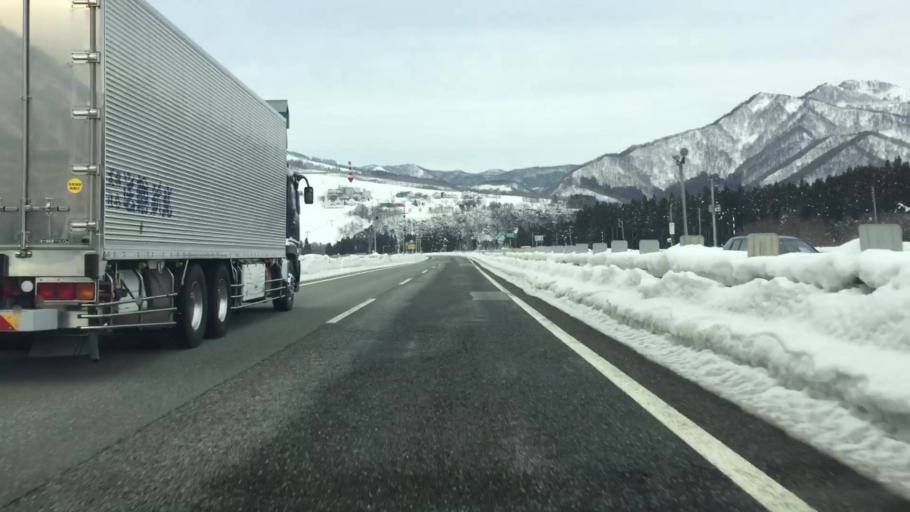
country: JP
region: Niigata
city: Shiozawa
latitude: 36.9197
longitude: 138.8405
